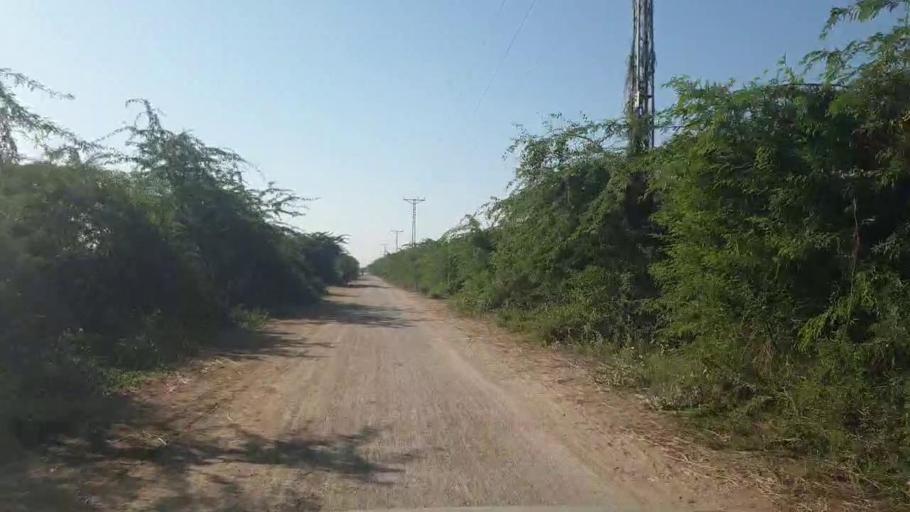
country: PK
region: Sindh
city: Rajo Khanani
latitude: 24.9501
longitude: 68.7942
